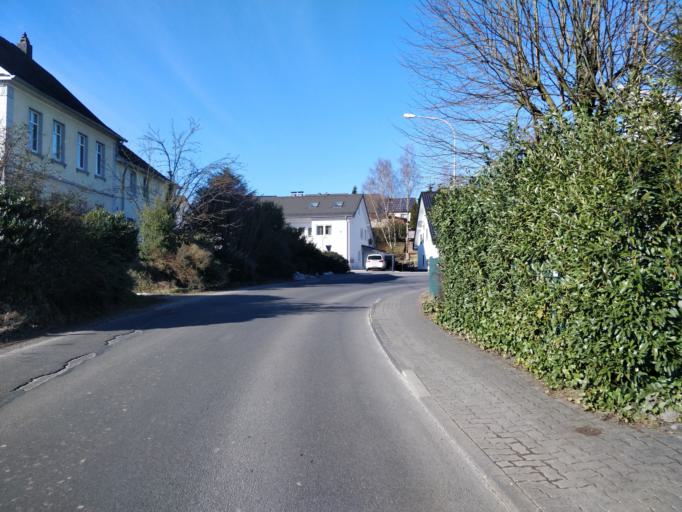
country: DE
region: North Rhine-Westphalia
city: Wiehl
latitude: 50.9290
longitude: 7.5519
